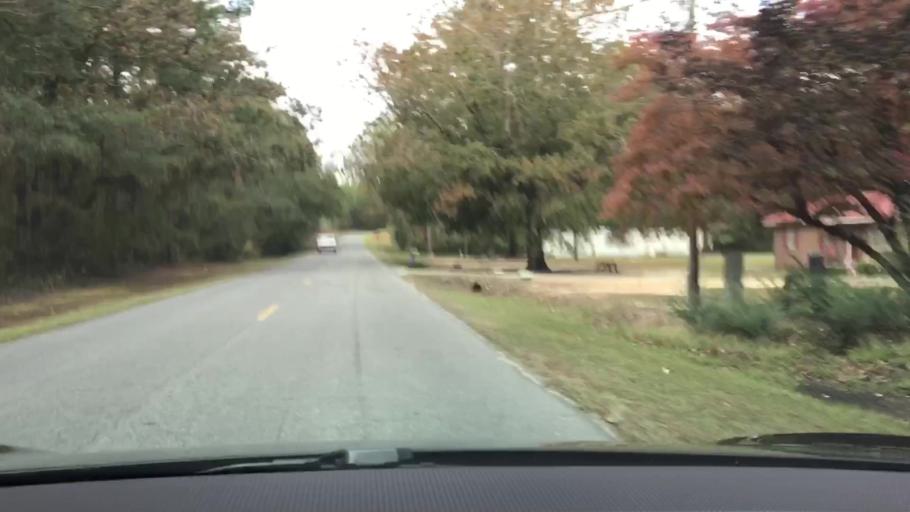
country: US
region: Georgia
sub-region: Jefferson County
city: Wadley
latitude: 32.7993
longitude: -82.3569
